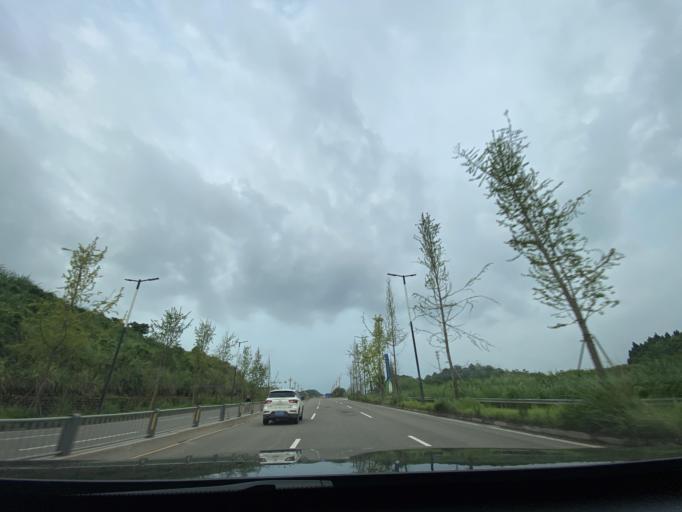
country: CN
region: Sichuan
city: Jiancheng
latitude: 30.4878
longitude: 104.4748
